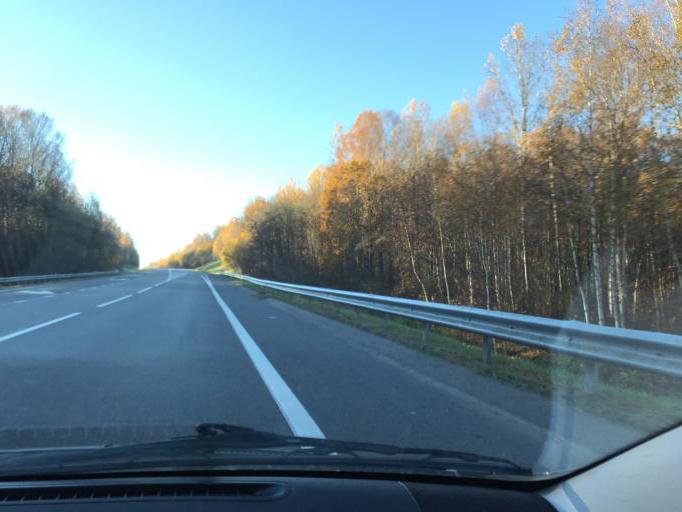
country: BY
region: Vitebsk
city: Vitebsk
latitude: 55.0266
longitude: 30.3240
